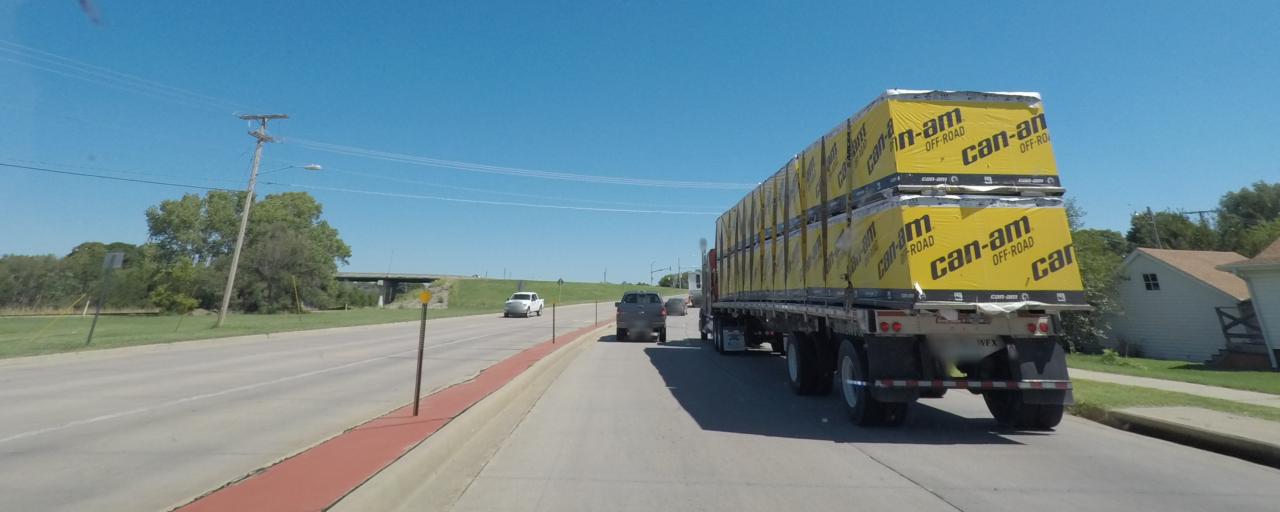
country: US
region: Kansas
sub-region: Sumner County
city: Wellington
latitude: 37.2658
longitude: -97.4038
